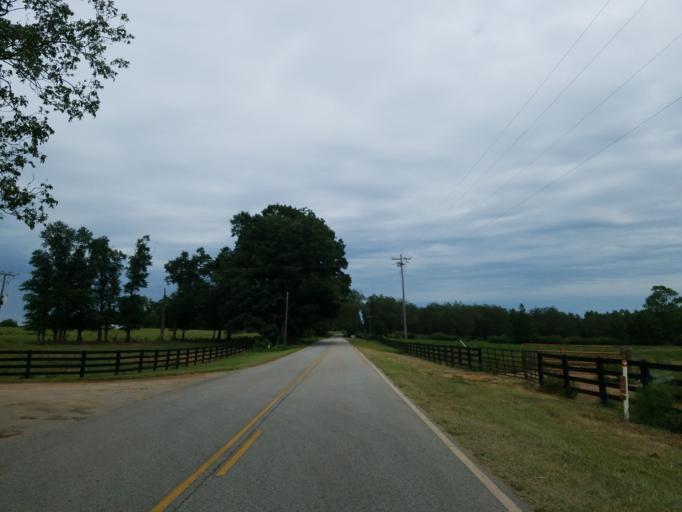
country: US
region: Georgia
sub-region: Lamar County
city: Barnesville
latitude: 33.0078
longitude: -84.0859
